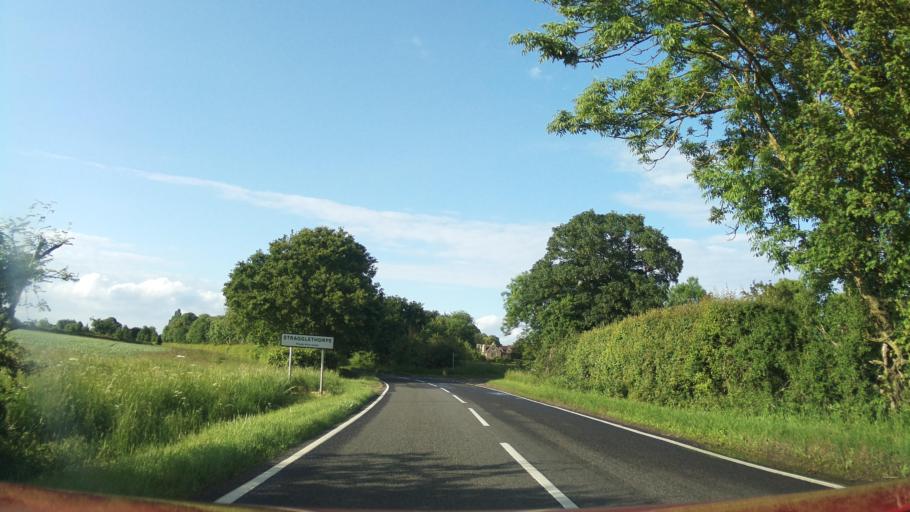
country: GB
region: England
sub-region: Lincolnshire
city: Great Gonerby
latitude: 53.0555
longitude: -0.6421
